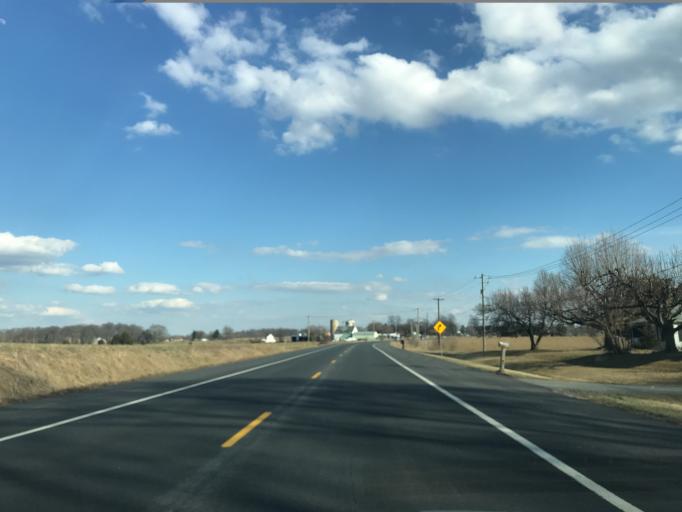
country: US
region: Maryland
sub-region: Cecil County
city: Rising Sun
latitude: 39.6773
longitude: -76.0288
